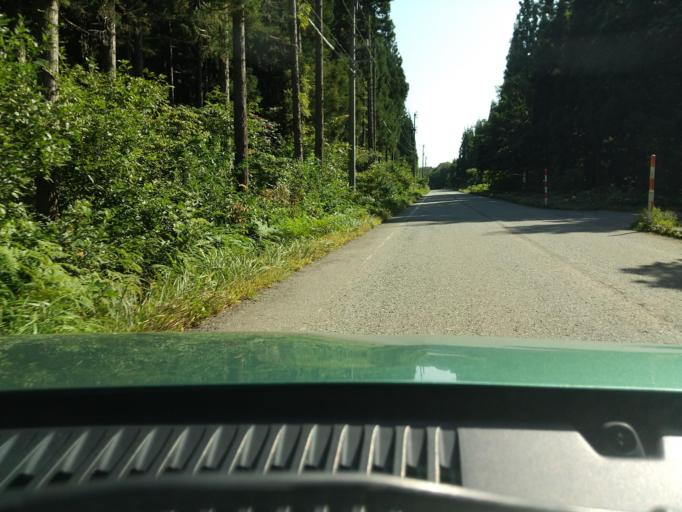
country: JP
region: Akita
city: Akita
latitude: 39.5979
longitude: 140.3080
